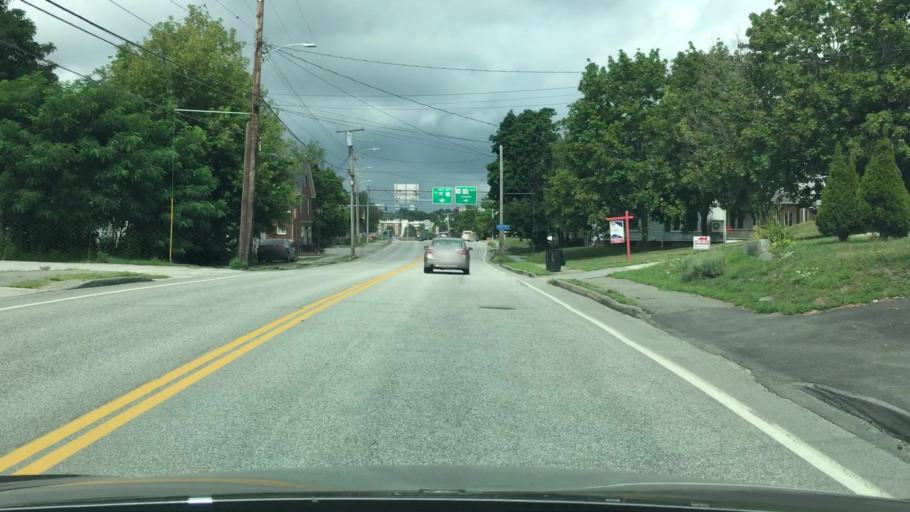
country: US
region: Maine
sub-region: Penobscot County
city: Brewer
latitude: 44.7957
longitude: -68.7603
